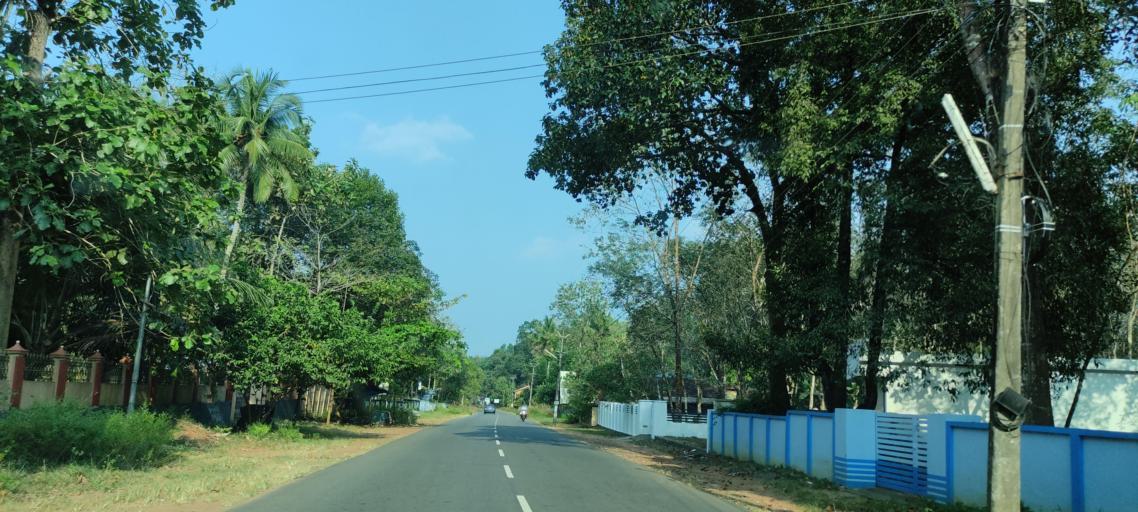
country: IN
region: Kerala
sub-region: Pattanamtitta
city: Adur
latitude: 9.0837
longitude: 76.6784
